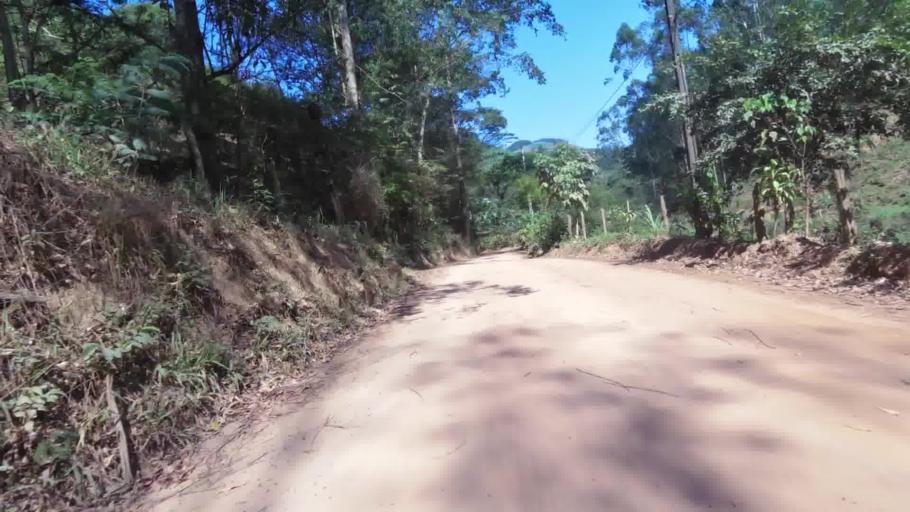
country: BR
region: Espirito Santo
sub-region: Alfredo Chaves
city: Alfredo Chaves
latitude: -20.6519
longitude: -40.8068
